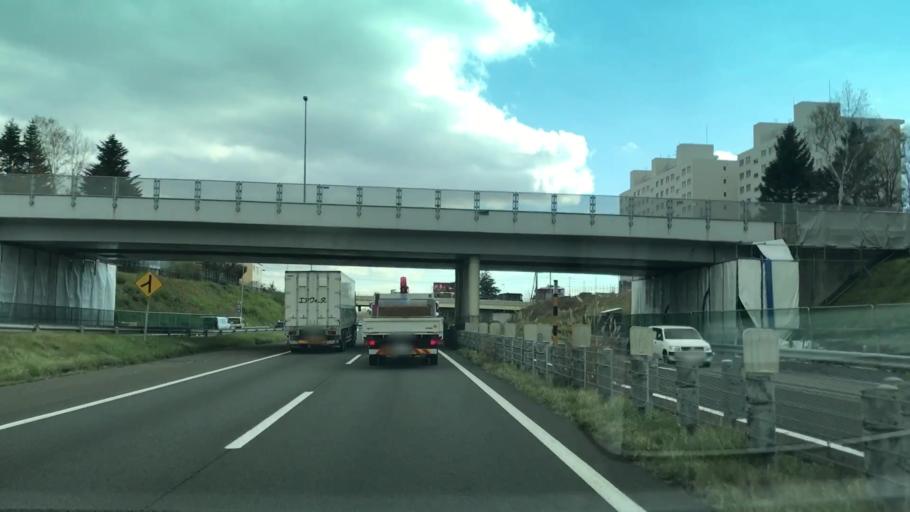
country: JP
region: Hokkaido
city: Kitahiroshima
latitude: 42.9771
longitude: 141.4782
